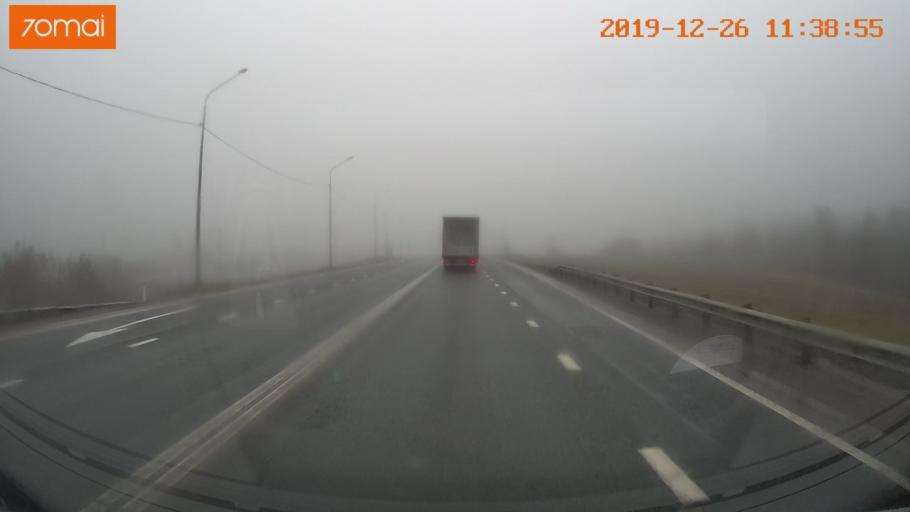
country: RU
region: Vologda
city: Sheksna
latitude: 59.2109
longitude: 38.6103
